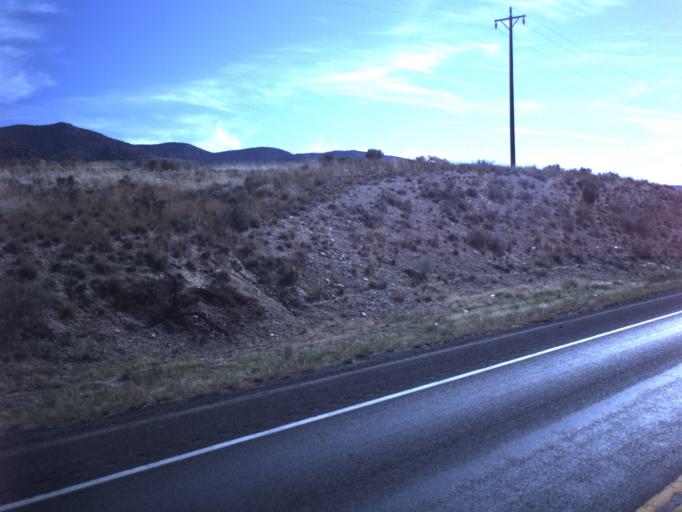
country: US
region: Utah
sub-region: Sanpete County
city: Gunnison
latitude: 39.2798
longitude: -111.8788
